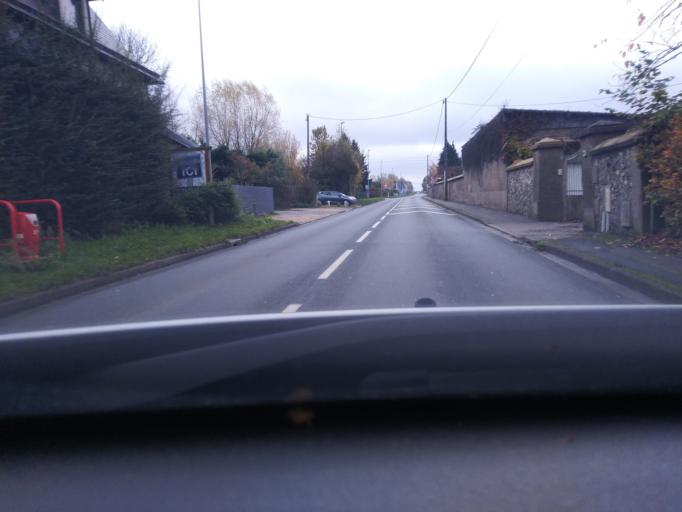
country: FR
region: Haute-Normandie
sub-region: Departement de la Seine-Maritime
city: La Vaupaliere
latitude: 49.4872
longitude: 1.0075
